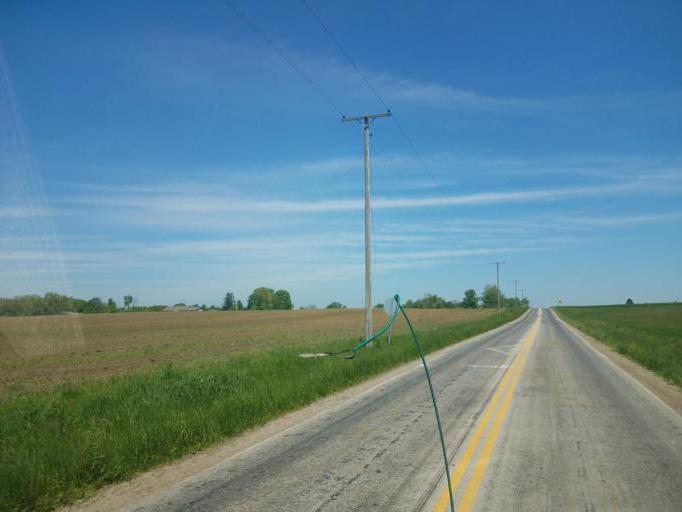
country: US
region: Ohio
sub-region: Ashland County
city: Ashland
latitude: 40.9348
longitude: -82.2434
